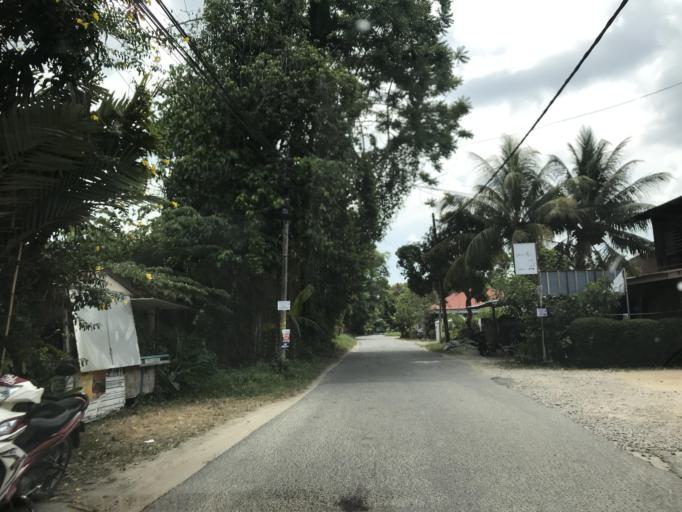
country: MY
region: Kelantan
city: Kota Bharu
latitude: 6.1349
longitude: 102.1827
